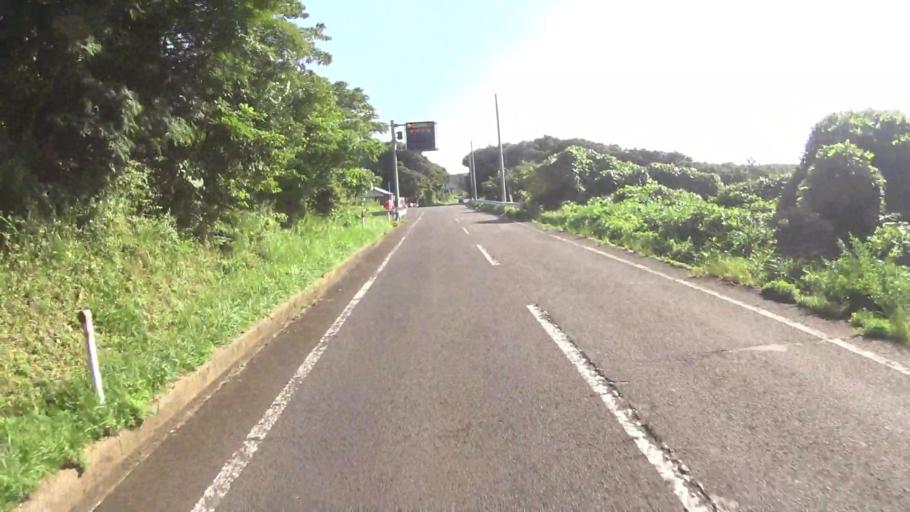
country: JP
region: Kyoto
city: Miyazu
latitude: 35.7085
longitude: 135.0695
